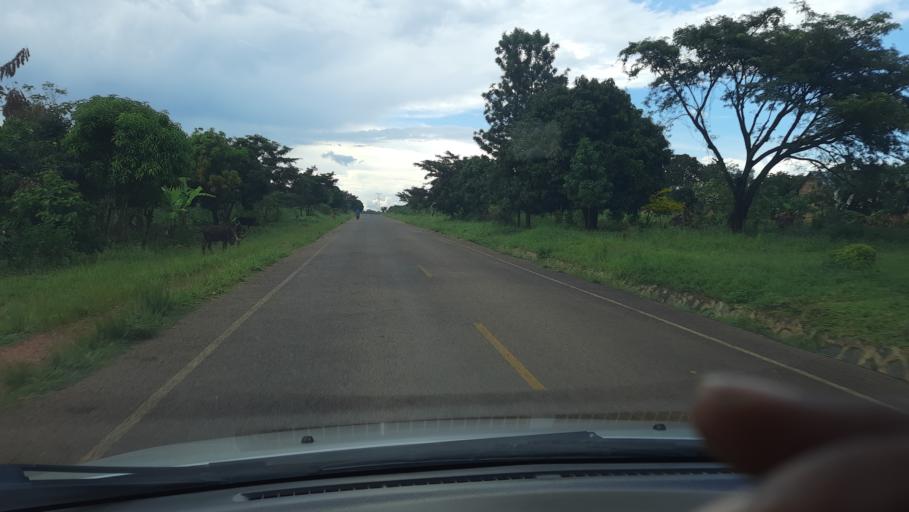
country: UG
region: Central Region
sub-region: Nakasongola District
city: Nakasongola
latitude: 1.3172
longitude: 32.4369
